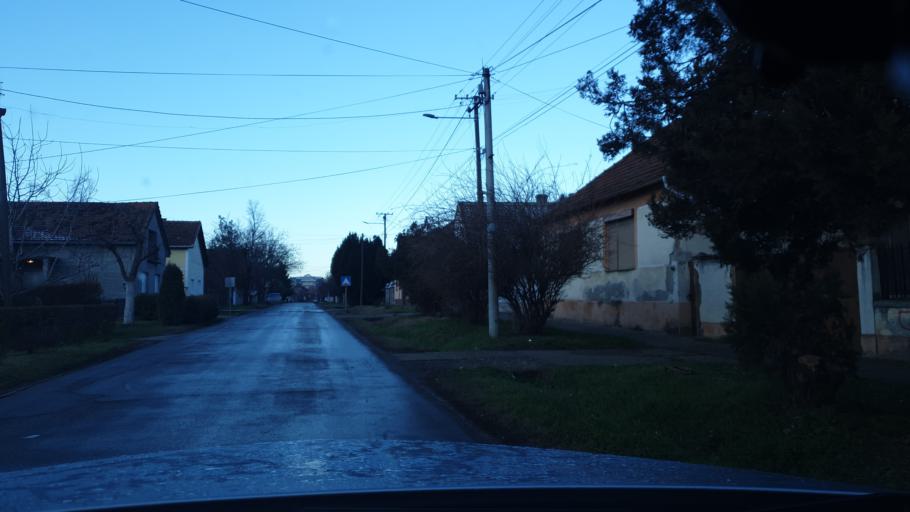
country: RS
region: Autonomna Pokrajina Vojvodina
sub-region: Sremski Okrug
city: Stara Pazova
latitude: 44.9881
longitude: 20.1685
